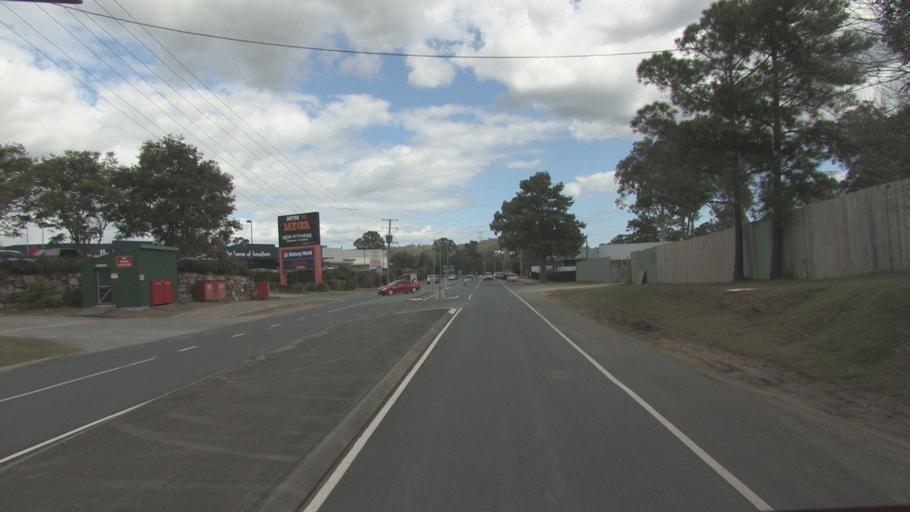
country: AU
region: Queensland
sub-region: Gold Coast
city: Yatala
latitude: -27.7232
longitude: 153.2151
